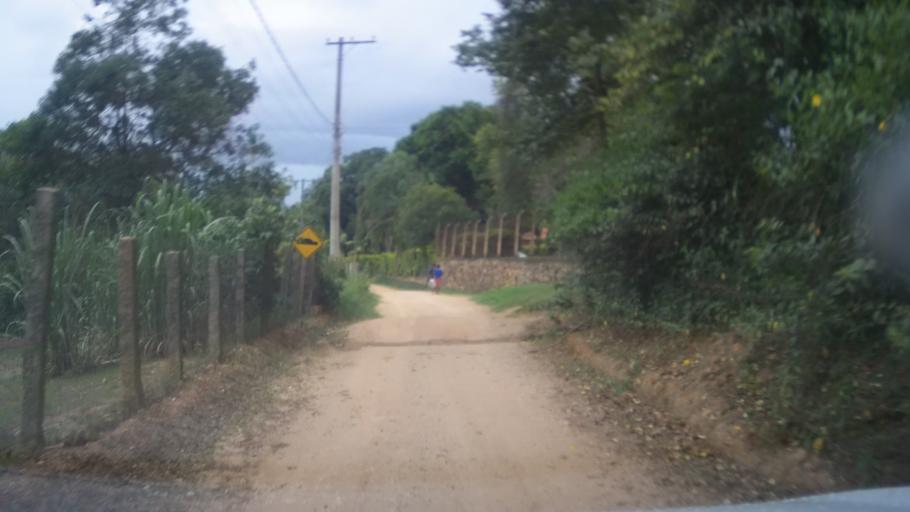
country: BR
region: Sao Paulo
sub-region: Itupeva
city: Itupeva
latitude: -23.1915
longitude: -47.0622
